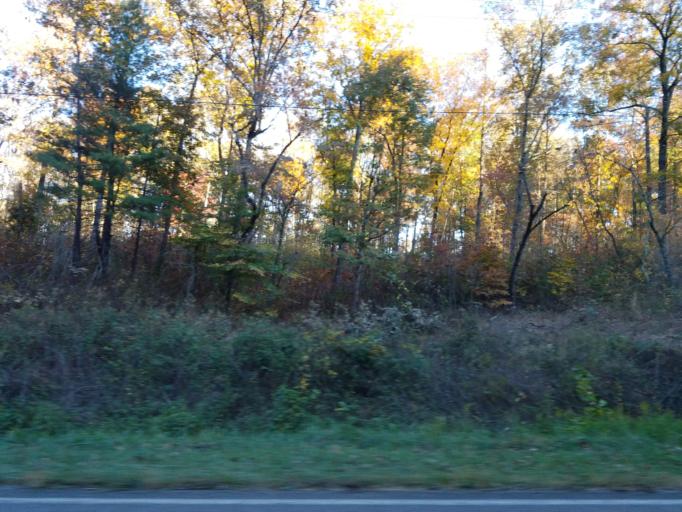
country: US
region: Georgia
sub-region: Gilmer County
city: Ellijay
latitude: 34.6106
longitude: -84.3956
